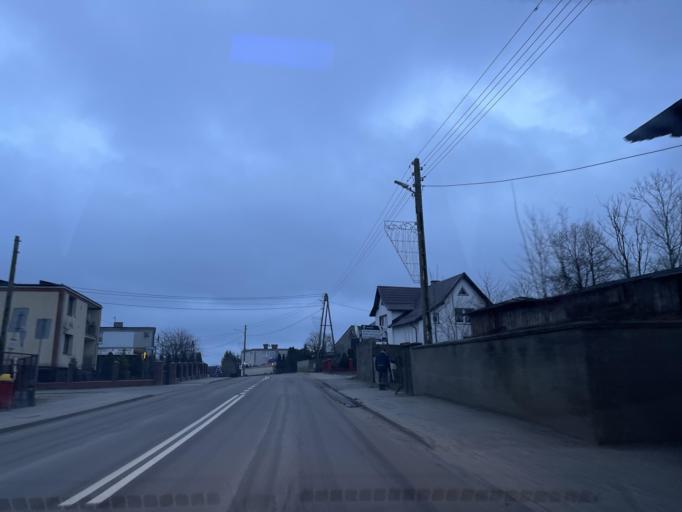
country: PL
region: Pomeranian Voivodeship
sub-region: Powiat wejherowski
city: Szemud
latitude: 54.4153
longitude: 18.1999
